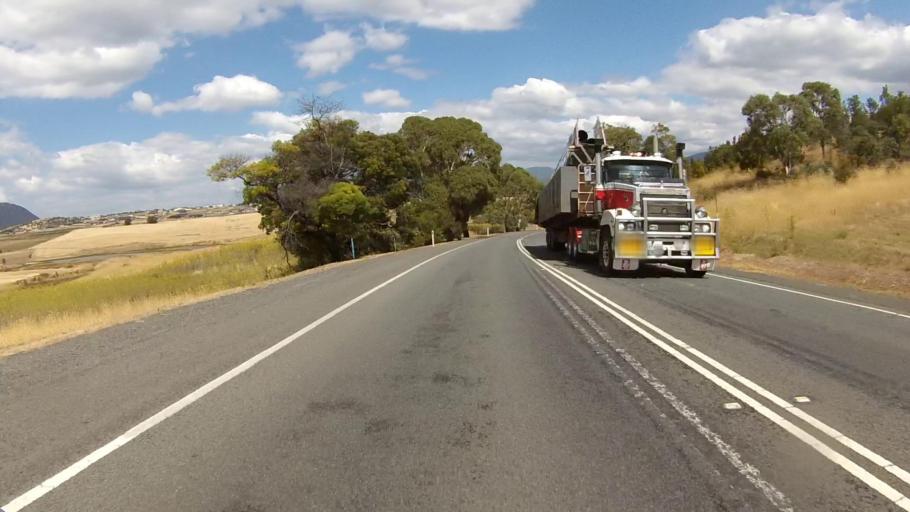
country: AU
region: Tasmania
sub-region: Brighton
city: Old Beach
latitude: -42.7529
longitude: 147.2722
